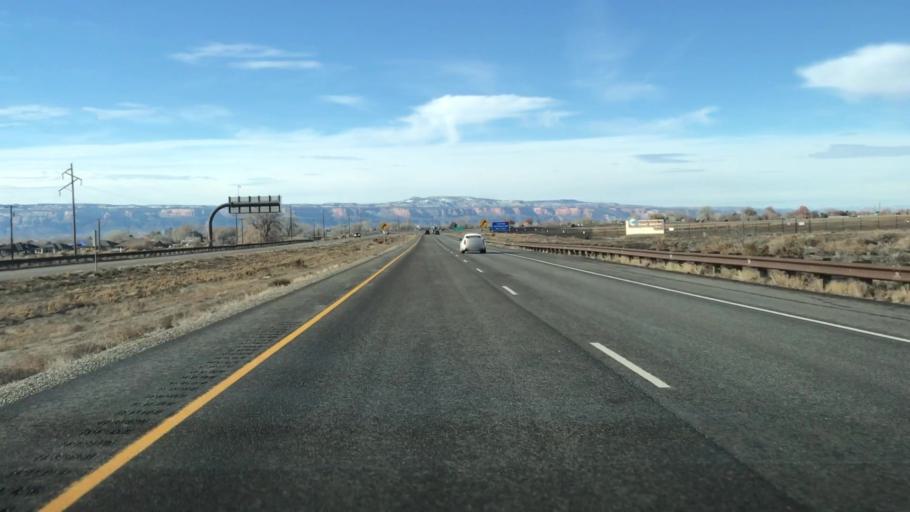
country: US
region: Colorado
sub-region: Mesa County
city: Fruitvale
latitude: 39.1060
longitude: -108.5246
